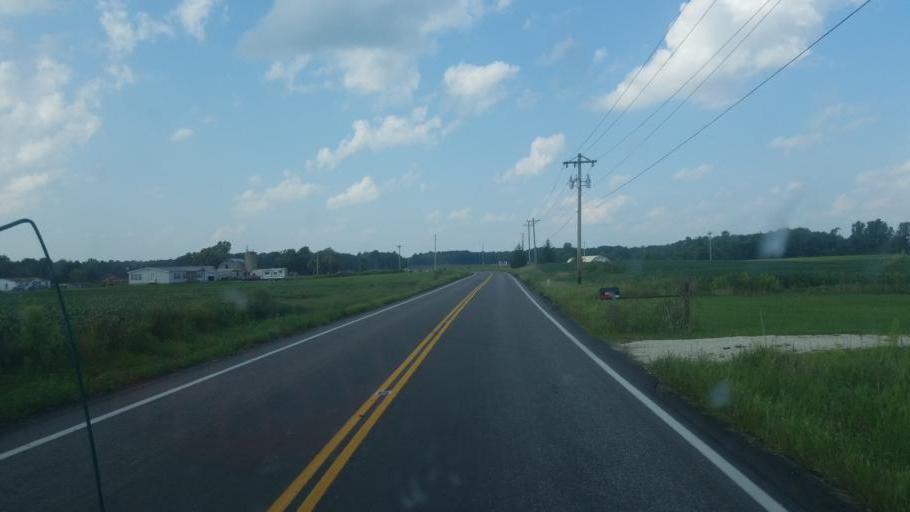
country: US
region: Ohio
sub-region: Wayne County
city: West Salem
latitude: 40.9619
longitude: -82.0861
